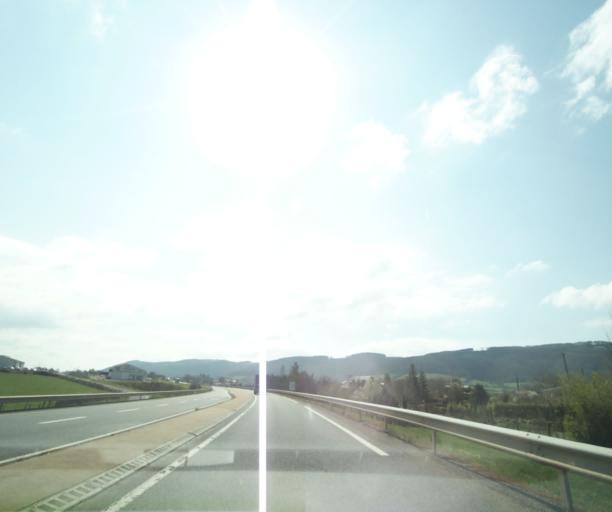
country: FR
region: Midi-Pyrenees
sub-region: Departement de l'Aveyron
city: Laissac
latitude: 44.3758
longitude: 2.8332
